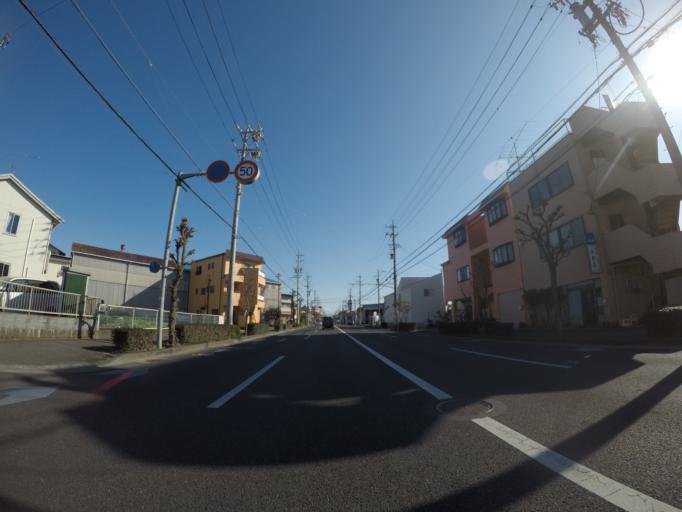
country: JP
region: Shizuoka
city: Shizuoka-shi
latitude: 35.0266
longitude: 138.4663
